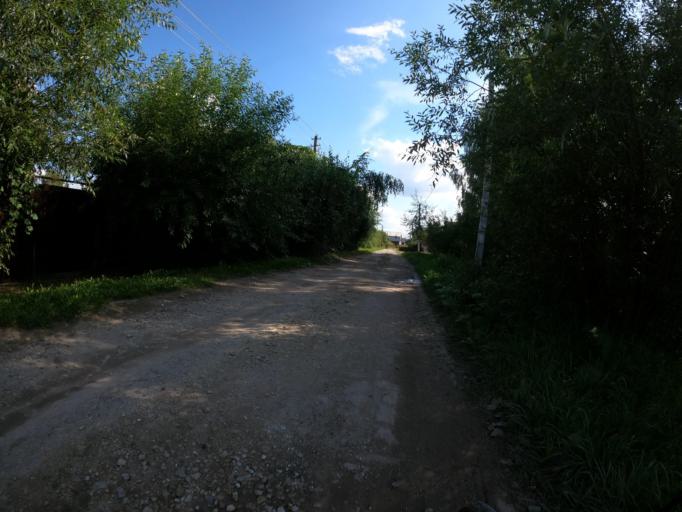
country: RU
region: Moskovskaya
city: Troitskoye
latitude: 55.2342
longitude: 38.4893
